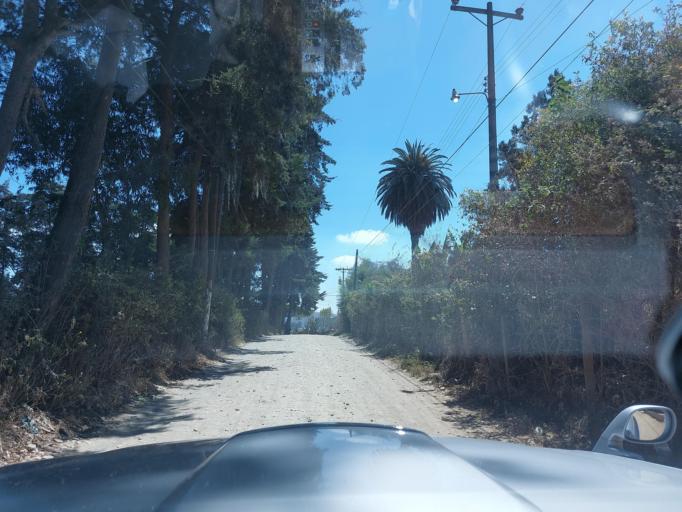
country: GT
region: Chimaltenango
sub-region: Municipio de Chimaltenango
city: Chimaltenango
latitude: 14.6559
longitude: -90.8273
